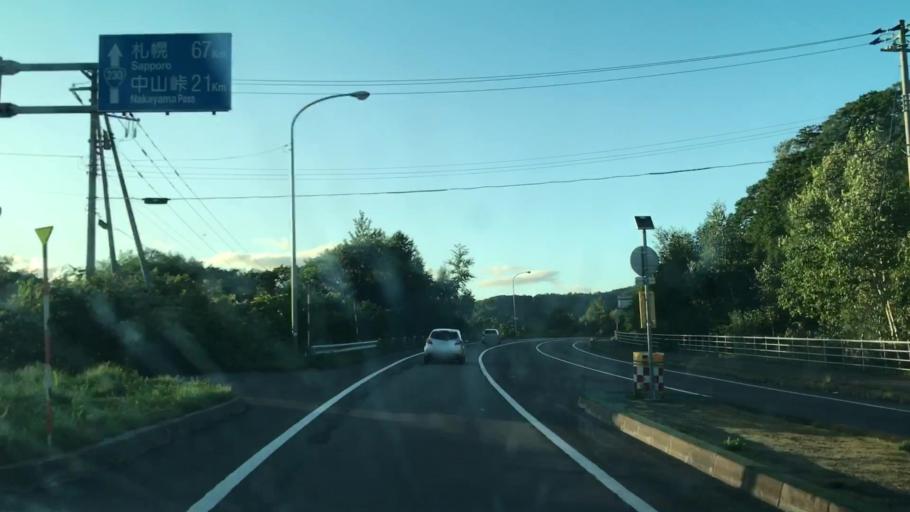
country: JP
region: Hokkaido
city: Niseko Town
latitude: 42.7899
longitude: 140.9357
